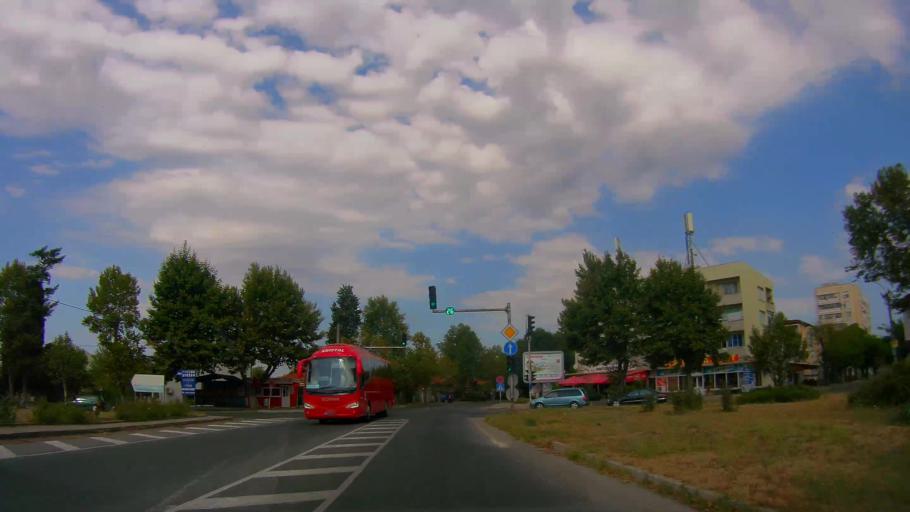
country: BG
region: Burgas
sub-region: Obshtina Aytos
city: Aytos
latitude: 42.6990
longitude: 27.2492
